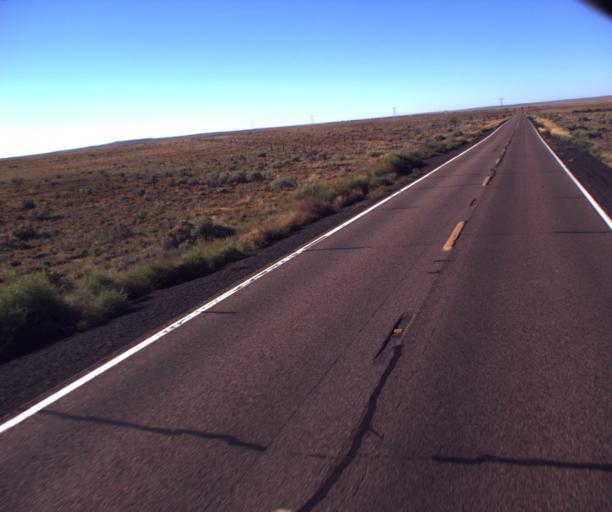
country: US
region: Arizona
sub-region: Navajo County
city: Holbrook
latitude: 34.8101
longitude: -110.2031
